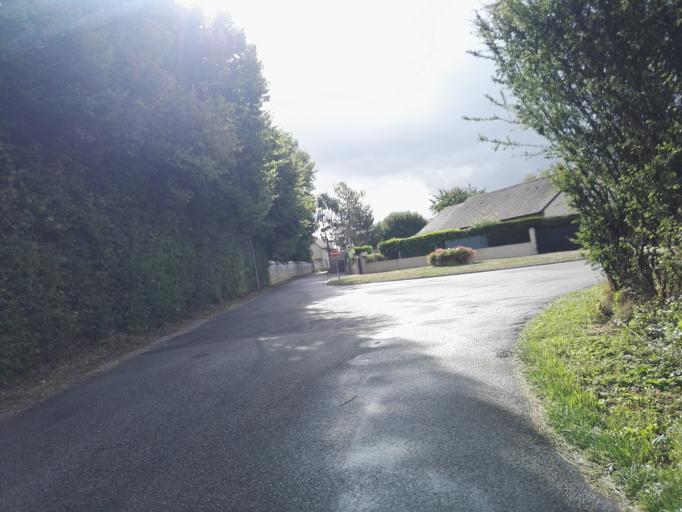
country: FR
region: Haute-Normandie
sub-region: Departement de l'Eure
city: Menilles
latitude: 49.0373
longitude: 1.3569
